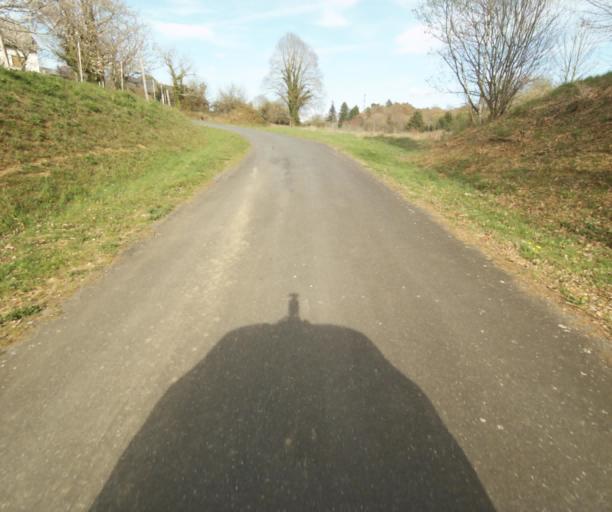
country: FR
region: Limousin
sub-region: Departement de la Correze
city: Naves
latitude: 45.3172
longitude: 1.7398
